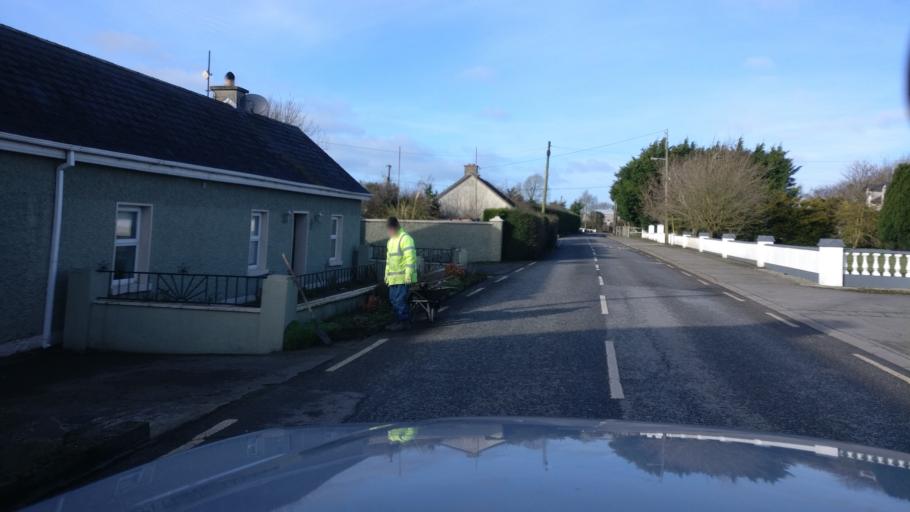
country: IE
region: Leinster
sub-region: Kilkenny
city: Castlecomer
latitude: 52.8612
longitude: -7.1635
